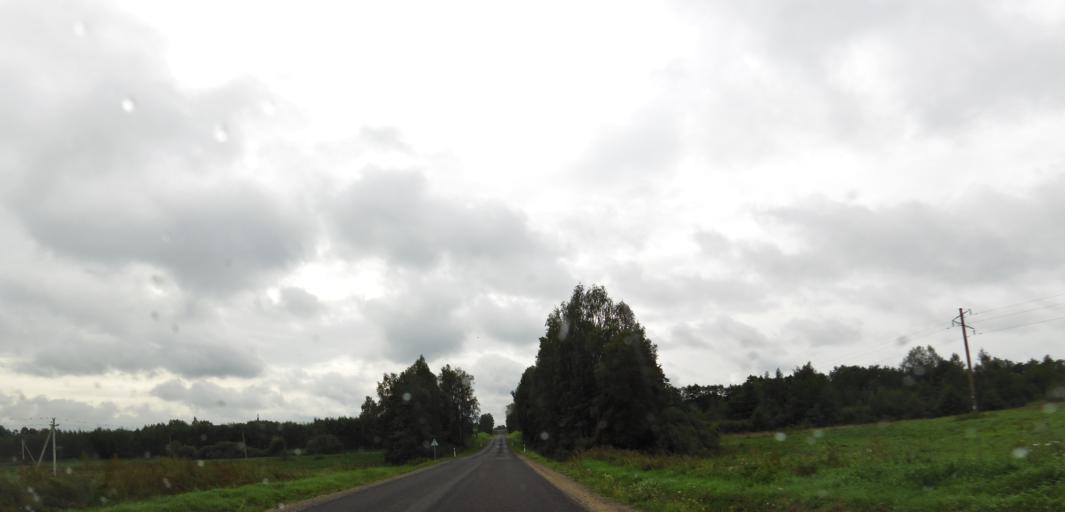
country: LT
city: Moletai
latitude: 55.2582
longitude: 25.3583
